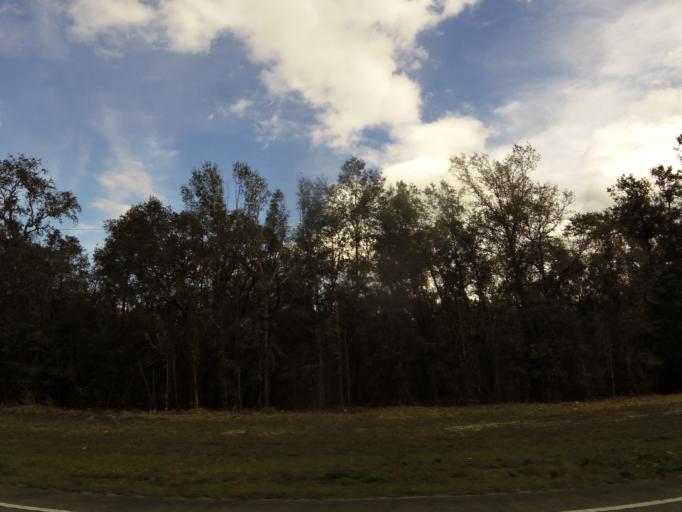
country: US
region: Florida
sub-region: Volusia County
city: De Leon Springs
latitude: 29.2375
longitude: -81.3248
